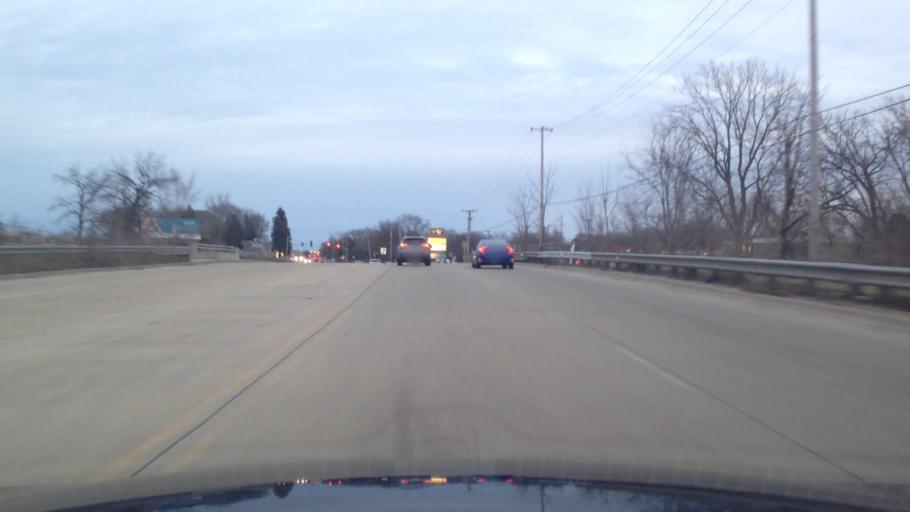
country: US
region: Illinois
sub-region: Lake County
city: Riverwoods
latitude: 42.1638
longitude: -87.9207
